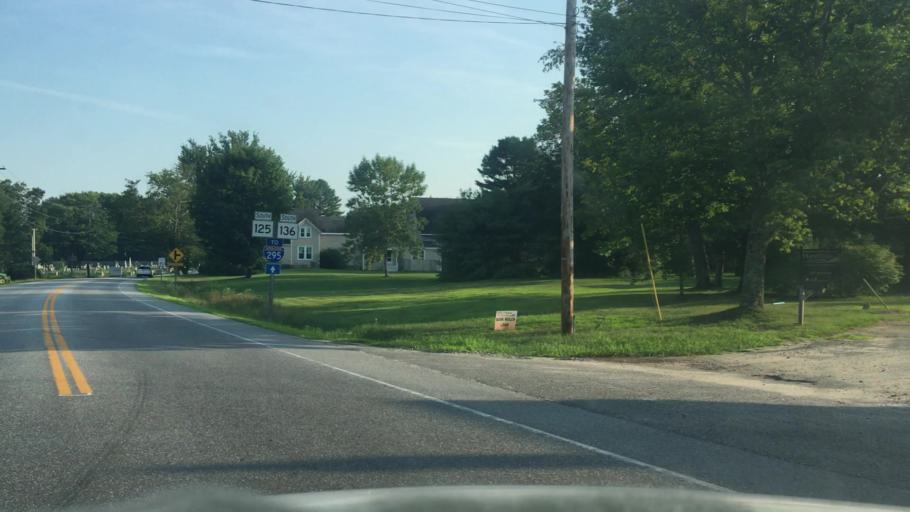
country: US
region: Maine
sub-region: Cumberland County
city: Freeport
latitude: 43.8756
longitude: -70.1068
